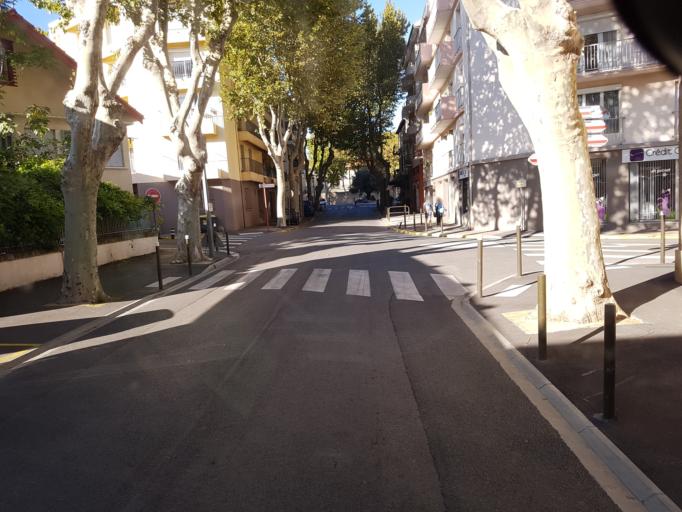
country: FR
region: Languedoc-Roussillon
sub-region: Departement de l'Aude
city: Narbonne
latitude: 43.1792
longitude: 3.0033
